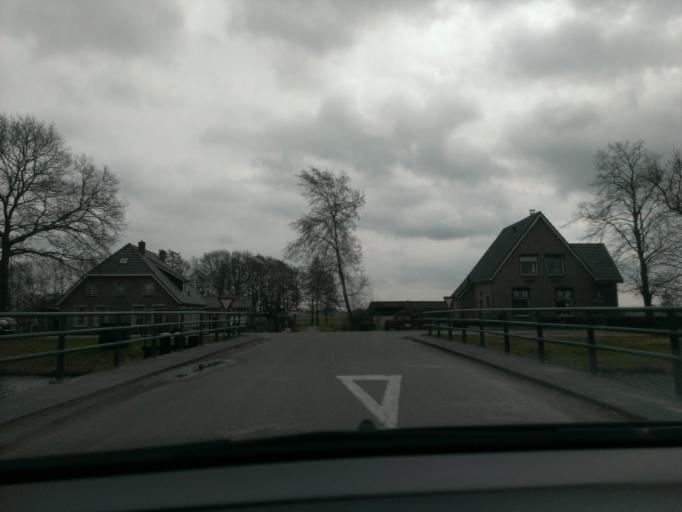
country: NL
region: Gelderland
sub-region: Gemeente Epe
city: Oene
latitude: 52.3616
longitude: 6.0321
